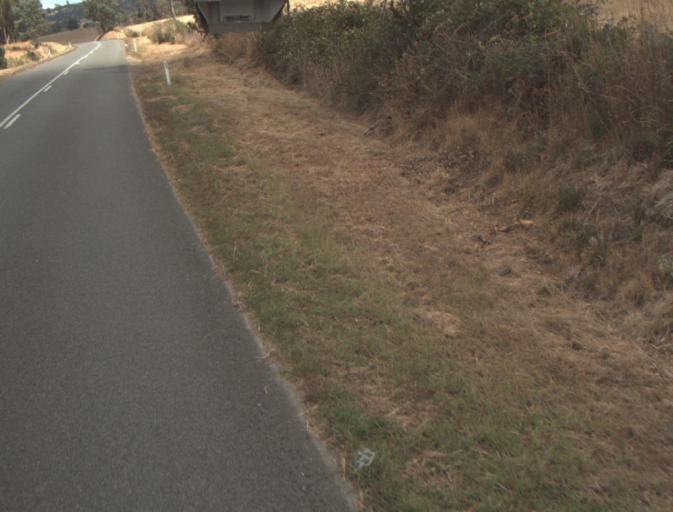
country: AU
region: Tasmania
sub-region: Launceston
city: Mayfield
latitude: -41.2182
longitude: 147.1216
